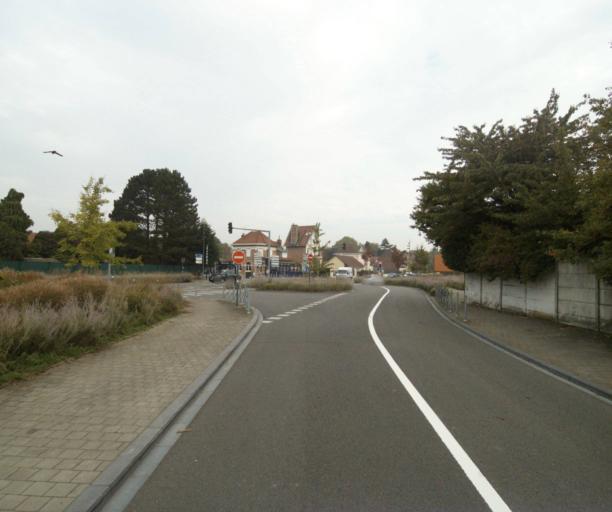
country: FR
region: Nord-Pas-de-Calais
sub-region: Departement du Nord
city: Seclin
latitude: 50.5428
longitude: 3.0223
